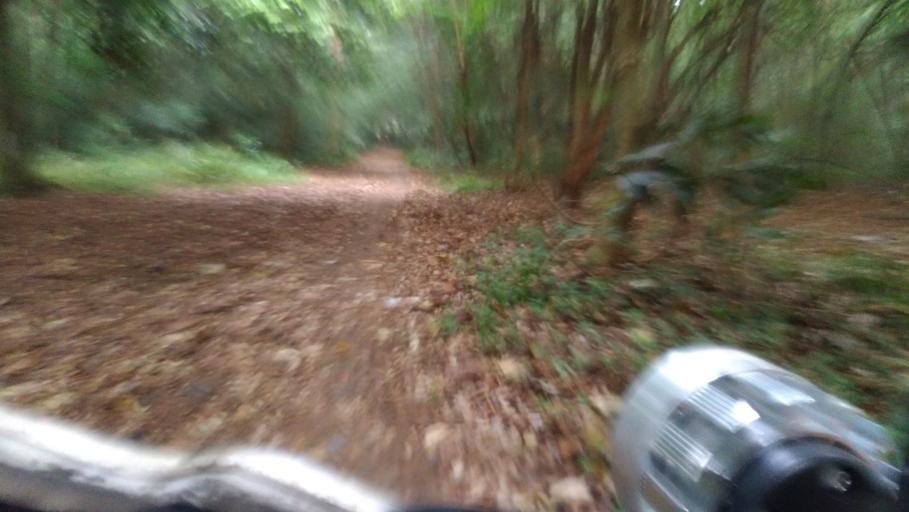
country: ID
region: West Java
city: Cileungsir
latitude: -6.3684
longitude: 106.9021
